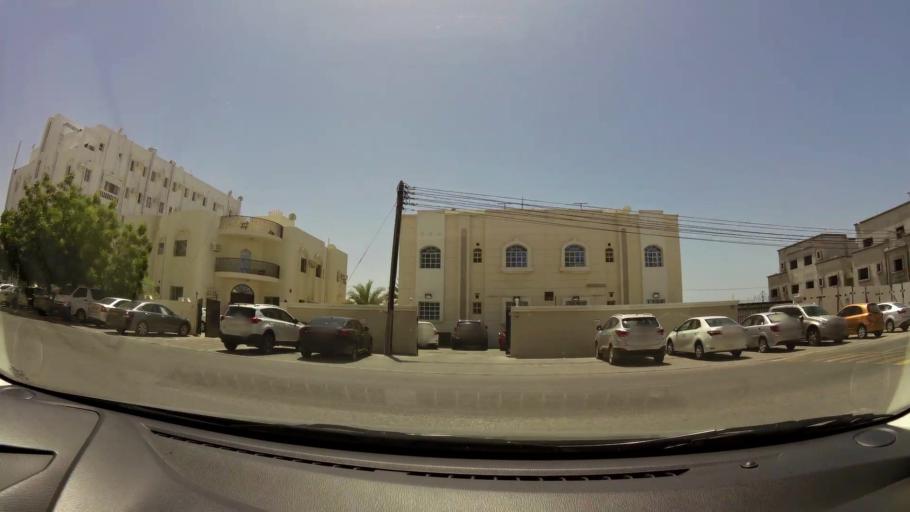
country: OM
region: Muhafazat Masqat
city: Bawshar
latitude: 23.5940
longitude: 58.3702
